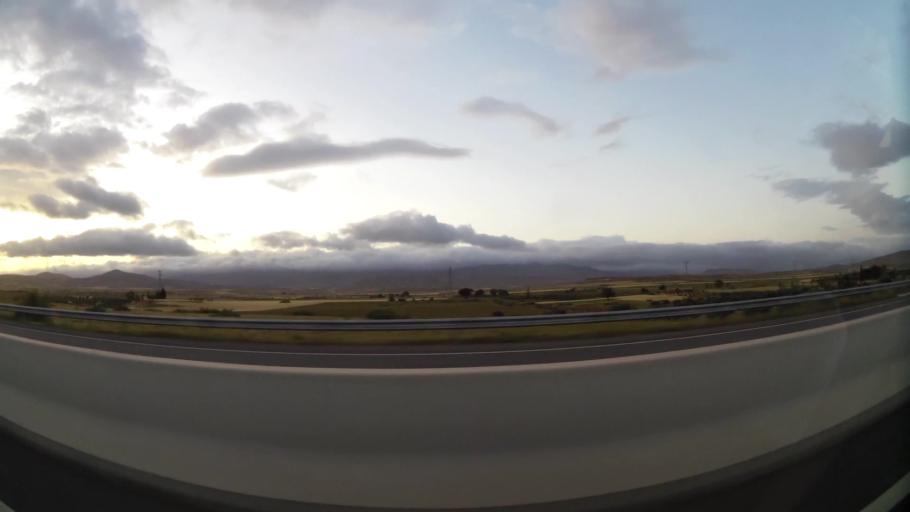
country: MA
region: Oriental
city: El Aioun
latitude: 34.6262
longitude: -2.5286
